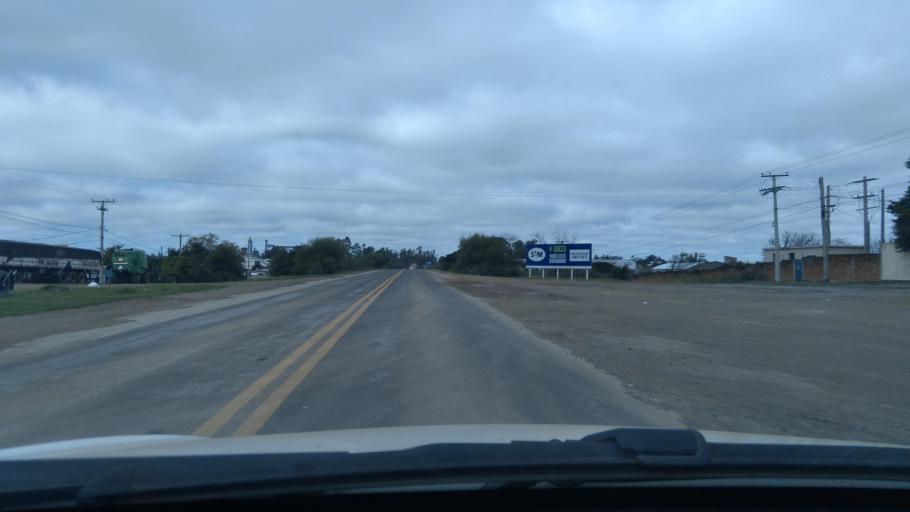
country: BR
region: Rio Grande do Sul
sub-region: Dom Pedrito
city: Dom Pedrito
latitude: -30.9722
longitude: -54.6538
